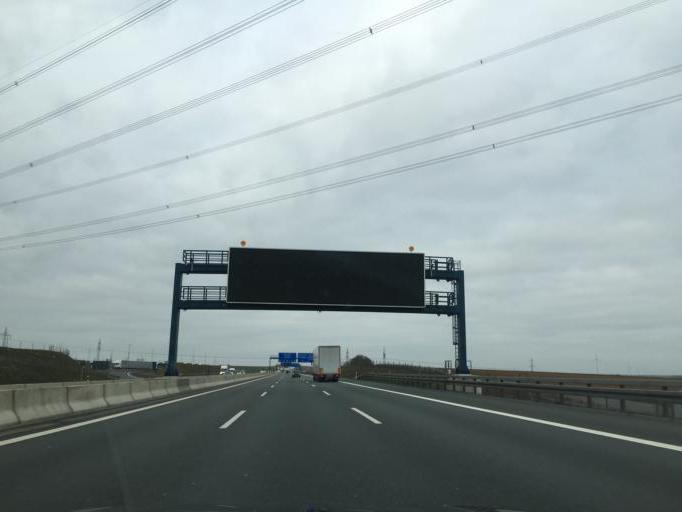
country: DE
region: Bavaria
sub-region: Regierungsbezirk Unterfranken
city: Theilheim
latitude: 49.7582
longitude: 10.0530
